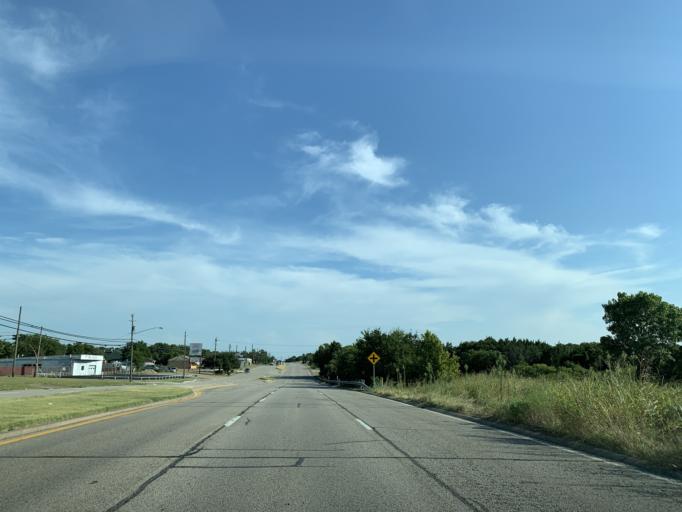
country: US
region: Texas
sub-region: Dallas County
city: Lancaster
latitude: 32.6573
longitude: -96.7833
